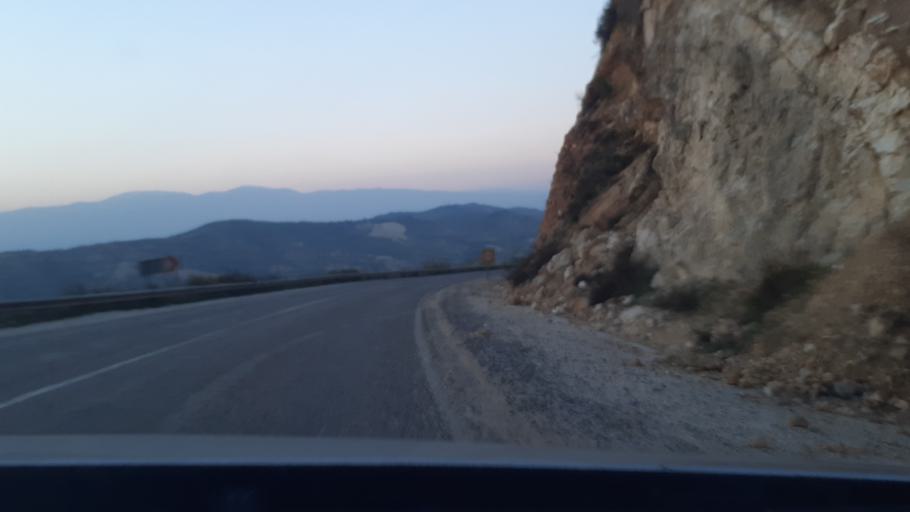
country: TR
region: Hatay
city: Dursunlu
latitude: 36.1689
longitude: 36.1864
